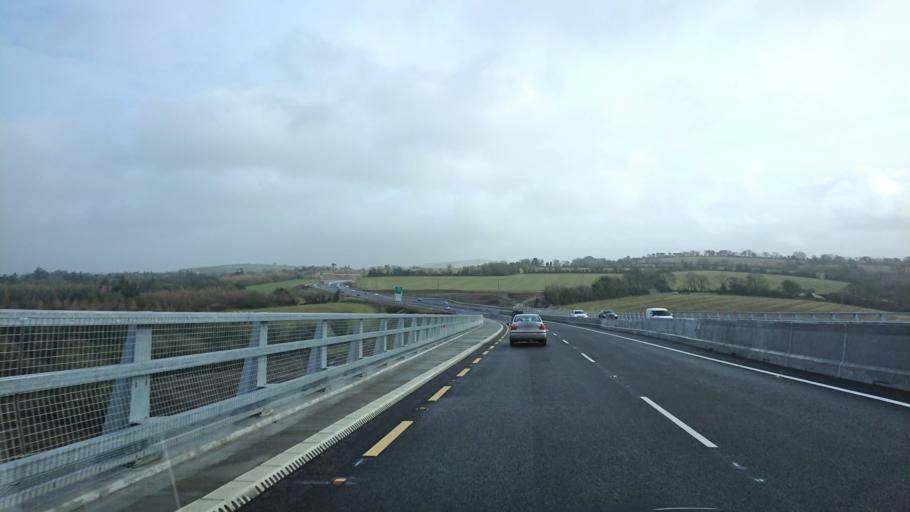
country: IE
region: Leinster
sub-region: Loch Garman
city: New Ross
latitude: 52.3577
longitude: -6.9883
